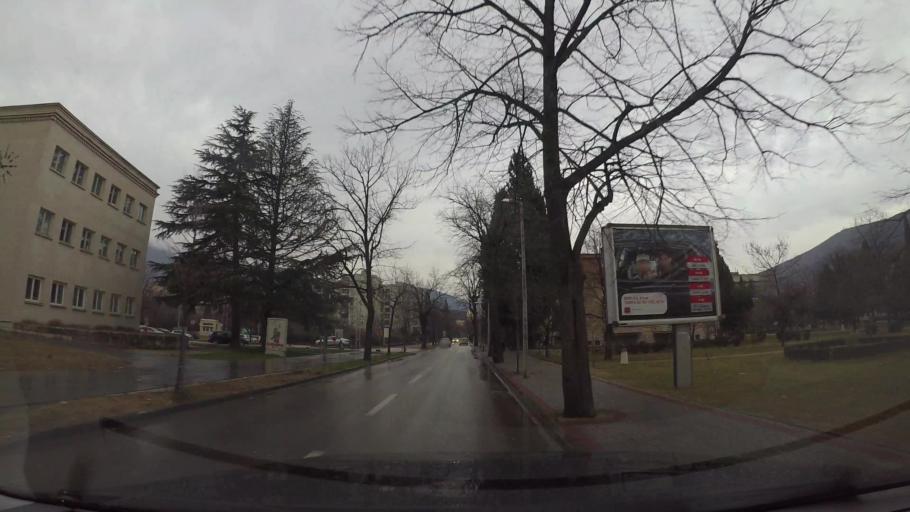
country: BA
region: Federation of Bosnia and Herzegovina
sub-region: Hercegovacko-Bosanski Kanton
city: Mostar
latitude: 43.3424
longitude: 17.8033
